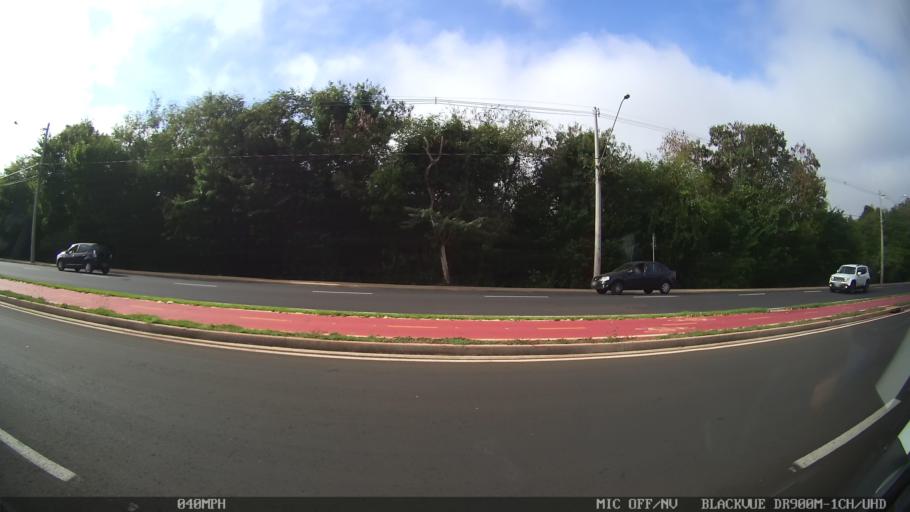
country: BR
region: Sao Paulo
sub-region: Sao Jose Do Rio Preto
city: Sao Jose do Rio Preto
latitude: -20.8120
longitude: -49.4334
